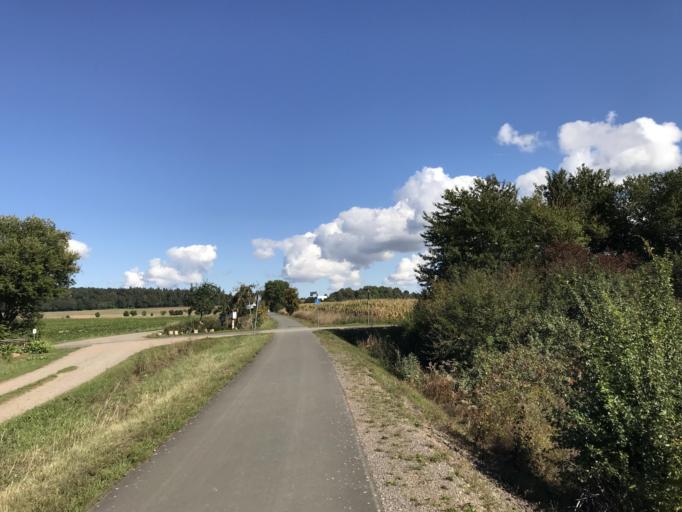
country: DE
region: Hesse
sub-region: Regierungsbezirk Kassel
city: Sachsenhausen
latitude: 51.2697
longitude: 8.9706
